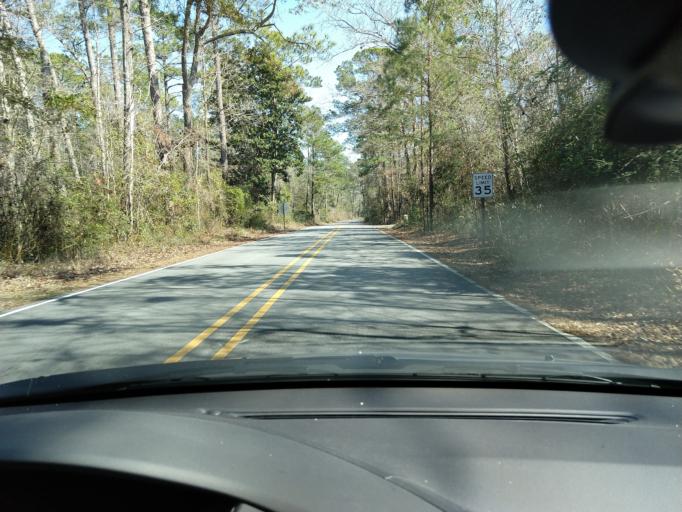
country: US
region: Mississippi
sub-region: Jackson County
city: Gulf Park Estates
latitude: 30.3960
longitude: -88.7869
